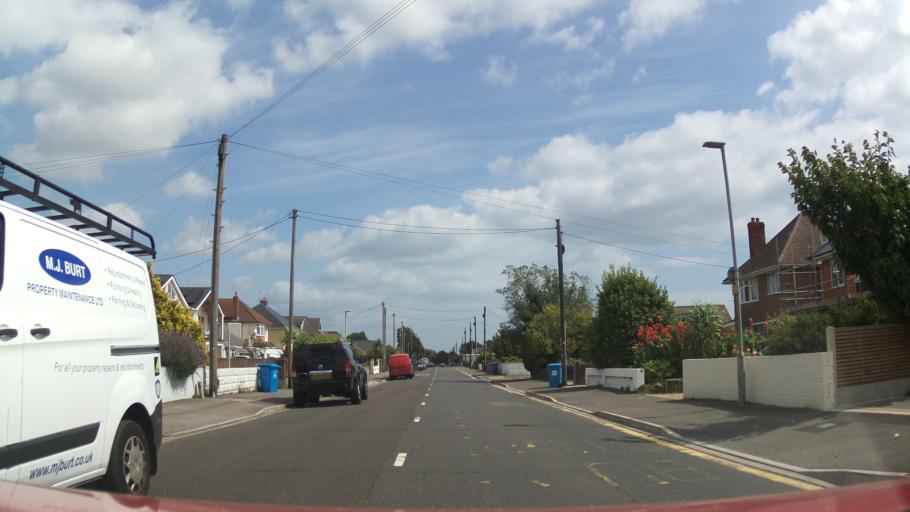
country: GB
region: England
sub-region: Poole
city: Poole
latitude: 50.7130
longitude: -2.0123
